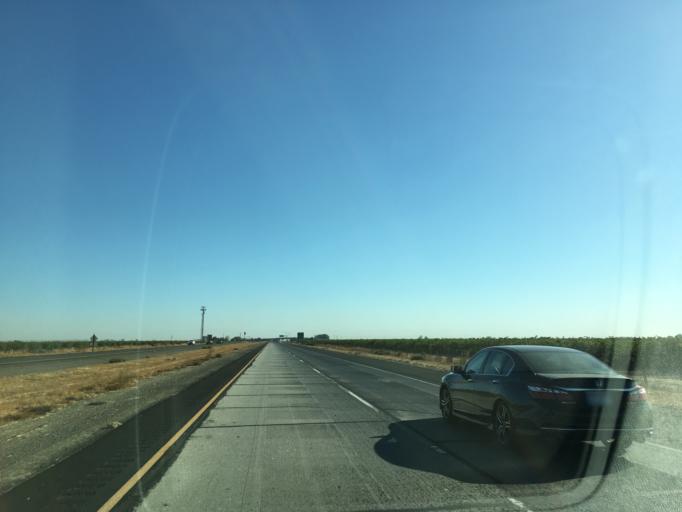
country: US
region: California
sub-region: Merced County
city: Dos Palos
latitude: 37.0781
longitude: -120.5061
